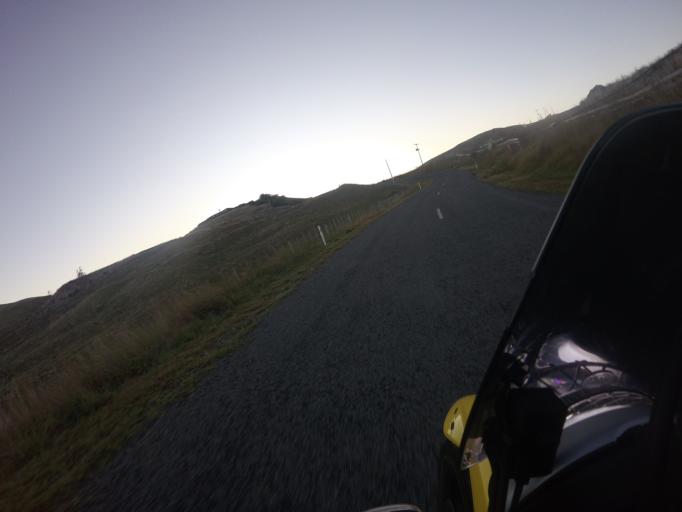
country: NZ
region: Gisborne
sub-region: Gisborne District
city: Gisborne
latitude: -38.6745
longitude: 178.0654
